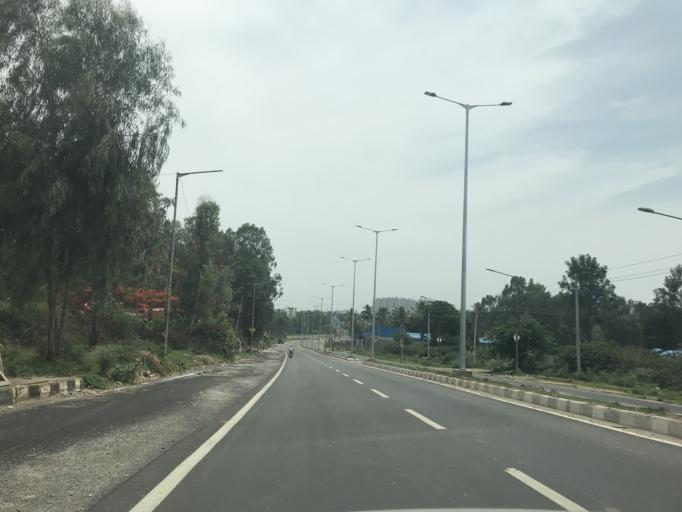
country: IN
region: Karnataka
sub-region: Bangalore Urban
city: Yelahanka
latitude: 13.1006
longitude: 77.6576
